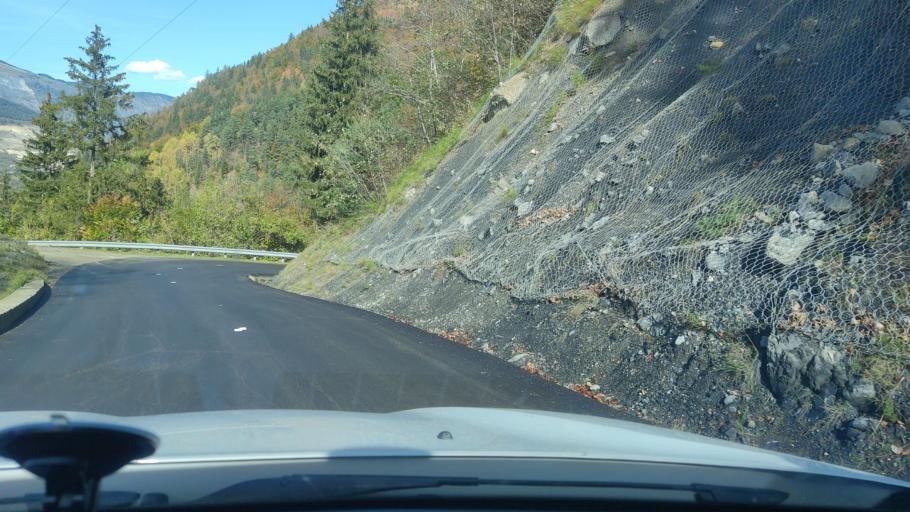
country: FR
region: Rhone-Alpes
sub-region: Departement de la Savoie
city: Saint-Jean-de-Maurienne
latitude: 45.2274
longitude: 6.3185
